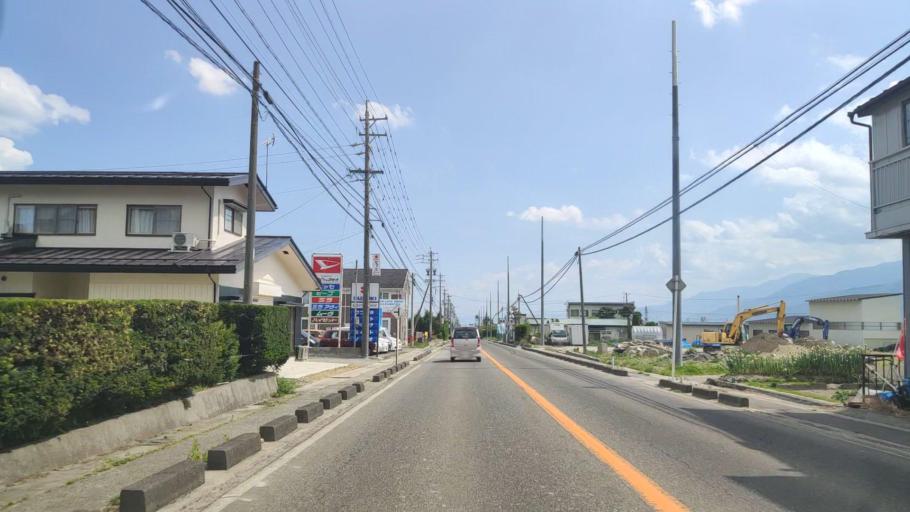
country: JP
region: Nagano
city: Omachi
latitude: 36.4635
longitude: 137.8498
